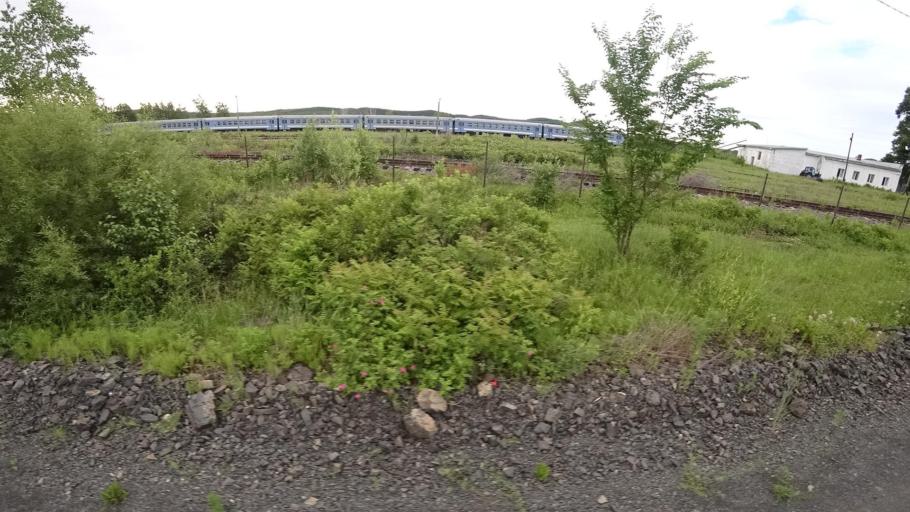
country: RU
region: Khabarovsk Krai
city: Amursk
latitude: 49.9069
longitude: 136.1472
